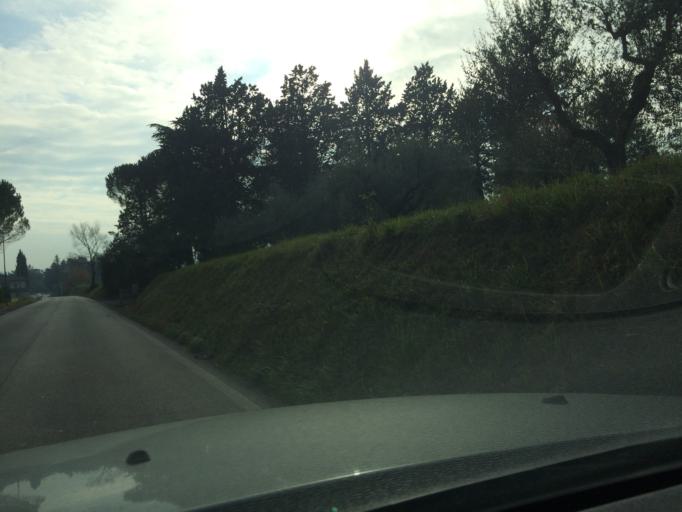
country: IT
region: Umbria
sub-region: Provincia di Perugia
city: Via Lippia
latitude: 43.0987
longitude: 12.4908
